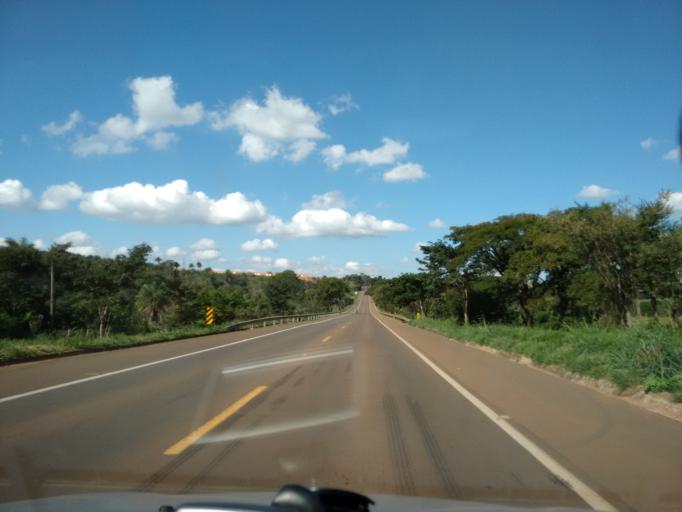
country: BR
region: Sao Paulo
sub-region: Sao Carlos
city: Sao Carlos
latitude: -22.0659
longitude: -47.9162
